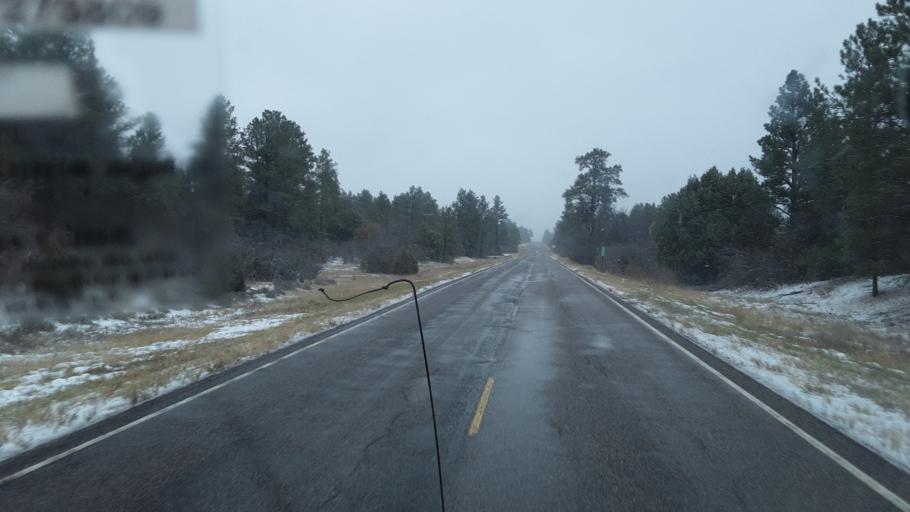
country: US
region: New Mexico
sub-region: Rio Arriba County
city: Tierra Amarilla
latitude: 36.6740
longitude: -106.5576
